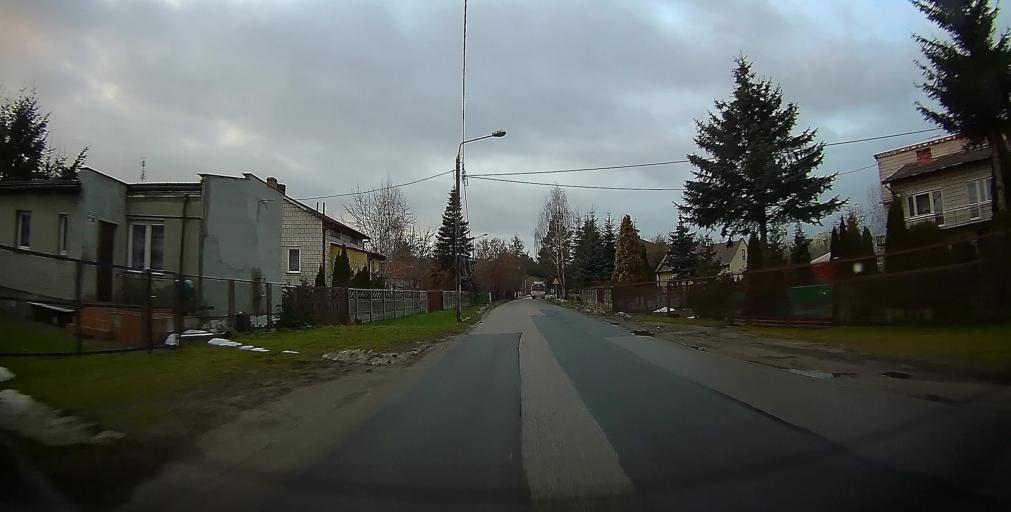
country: PL
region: Masovian Voivodeship
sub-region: Radom
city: Radom
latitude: 51.4496
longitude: 21.1364
